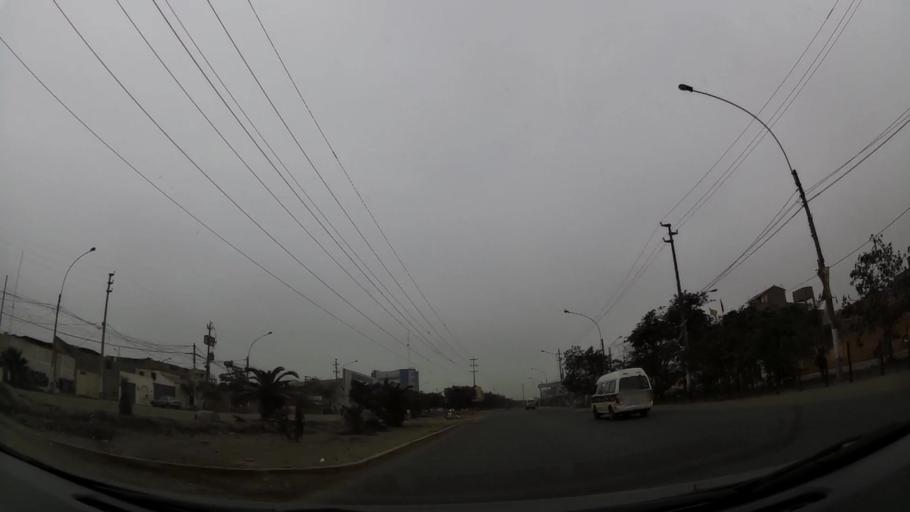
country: PE
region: Lima
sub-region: Lima
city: Urb. Santo Domingo
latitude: -11.8944
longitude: -77.0470
